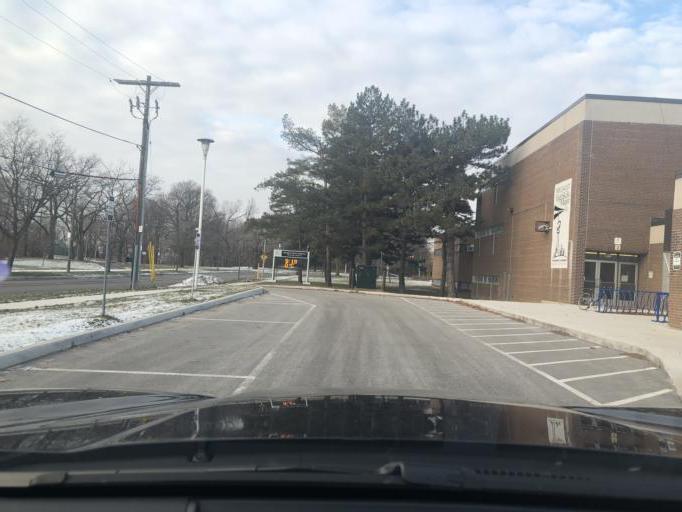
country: CA
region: Ontario
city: Willowdale
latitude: 43.7637
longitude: -79.3399
